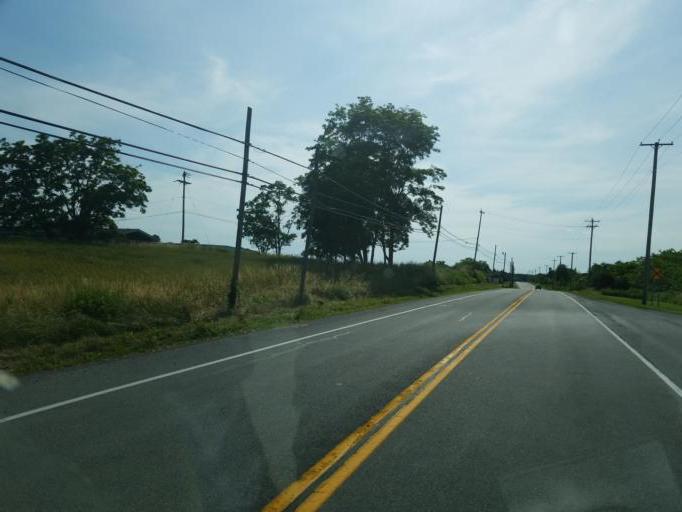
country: US
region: New York
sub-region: Livingston County
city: Caledonia
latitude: 42.9776
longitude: -77.8798
